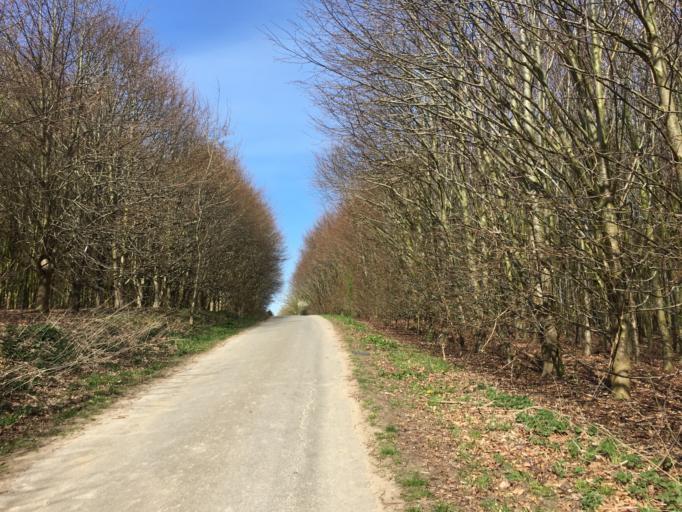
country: DE
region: Schleswig-Holstein
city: Nottfeld
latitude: 54.5899
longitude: 9.8011
